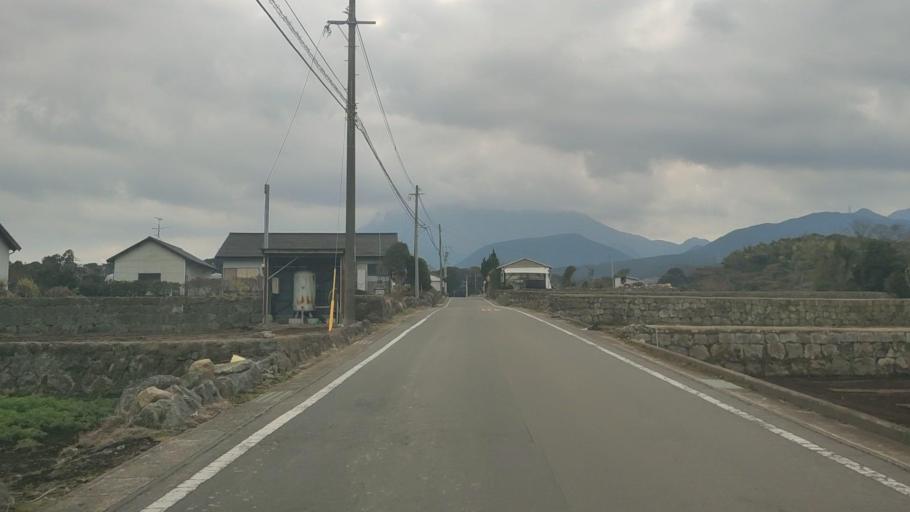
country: JP
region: Nagasaki
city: Shimabara
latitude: 32.8306
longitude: 130.2918
